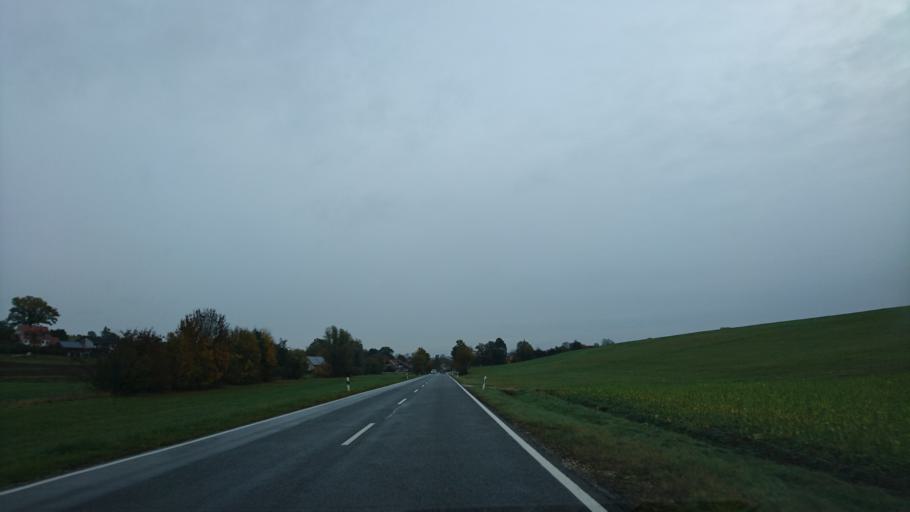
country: DE
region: Bavaria
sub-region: Regierungsbezirk Mittelfranken
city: Heideck
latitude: 49.1078
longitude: 11.1538
